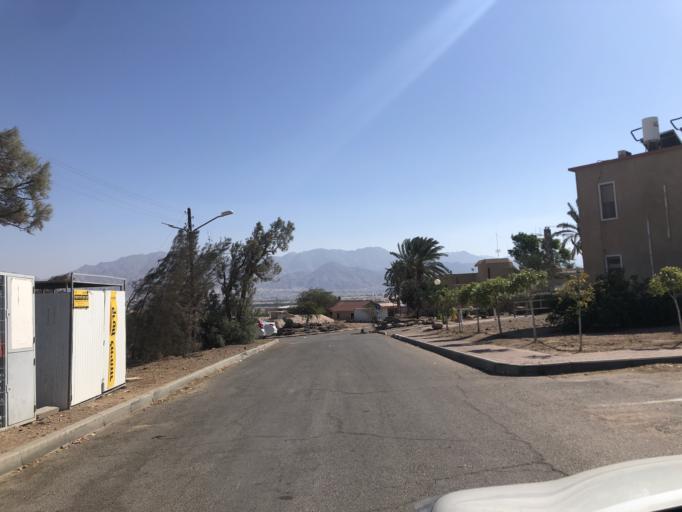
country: IL
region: Southern District
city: Eilat
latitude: 29.5829
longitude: 34.9629
